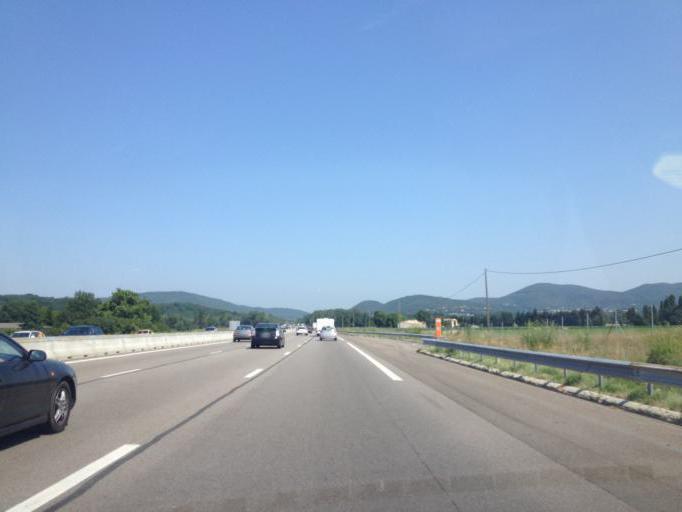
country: FR
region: Rhone-Alpes
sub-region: Departement de la Drome
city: Saint-Marcel-les-Sauzet
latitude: 44.5726
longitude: 4.8086
